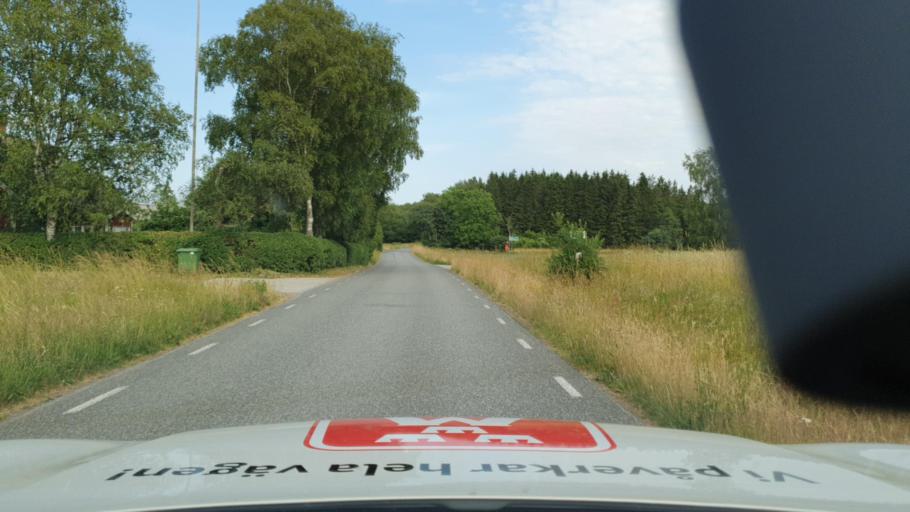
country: SE
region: Skane
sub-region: Kristianstads Kommun
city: Degeberga
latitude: 55.6898
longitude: 14.0910
